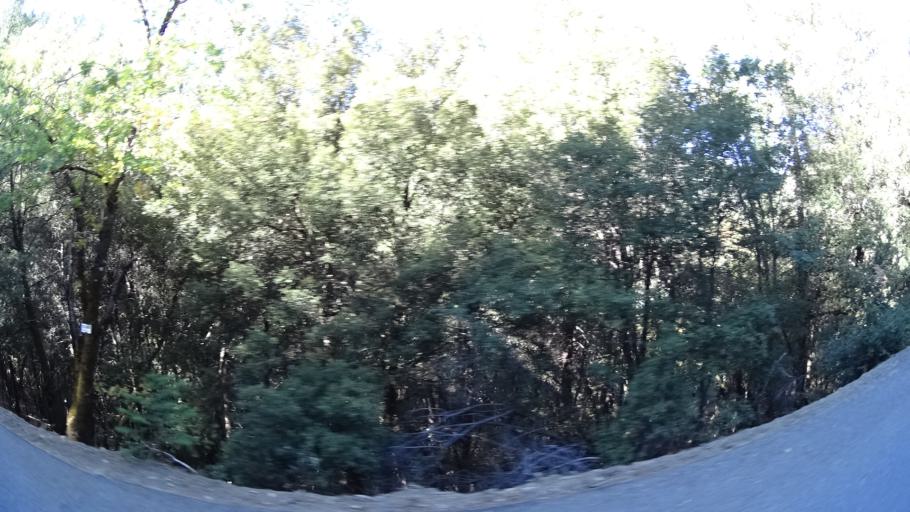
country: US
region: California
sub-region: Humboldt County
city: Willow Creek
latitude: 41.1665
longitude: -123.2141
